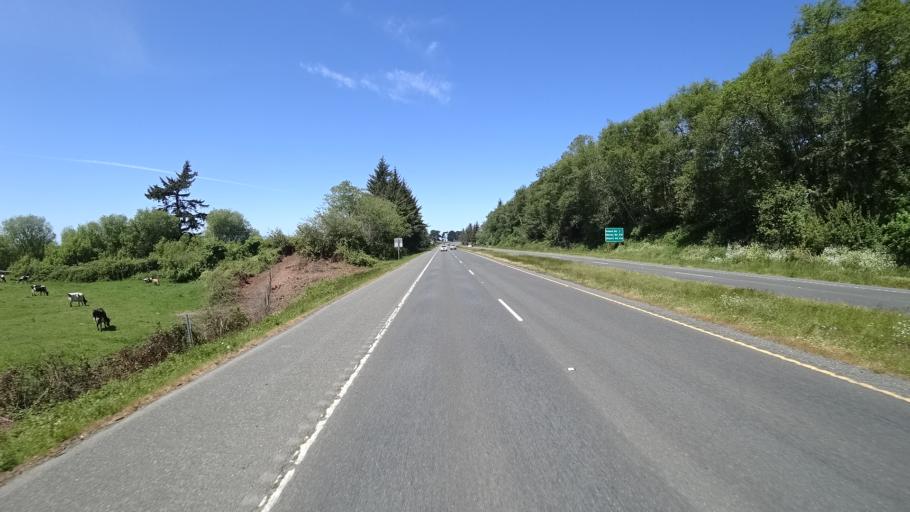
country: US
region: California
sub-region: Humboldt County
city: McKinleyville
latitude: 40.9237
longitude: -124.1049
